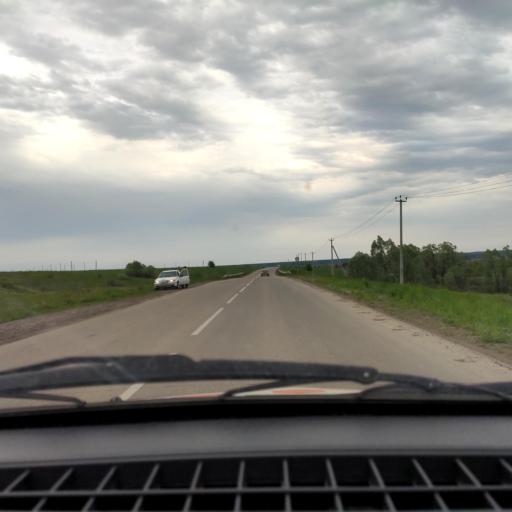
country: RU
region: Bashkortostan
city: Avdon
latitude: 54.5658
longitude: 55.7594
